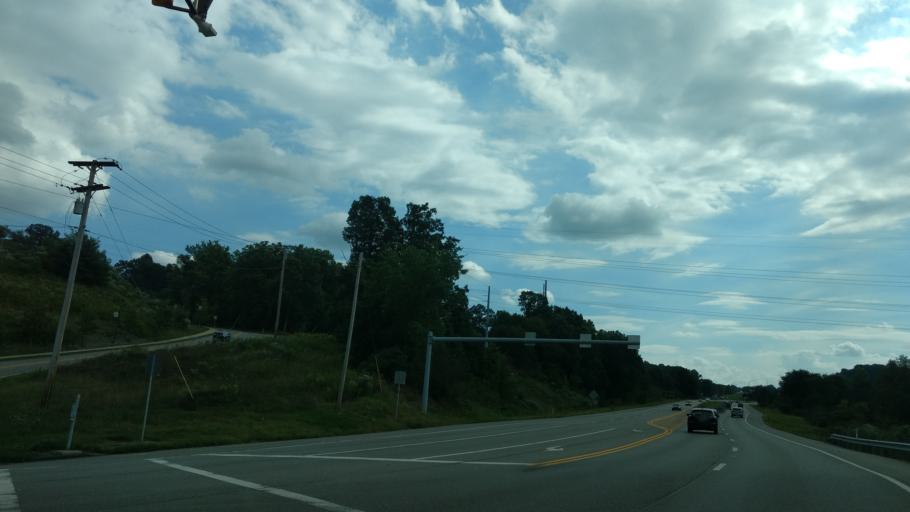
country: US
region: Pennsylvania
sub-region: Allegheny County
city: Bradford Woods
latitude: 40.6546
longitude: -80.0917
